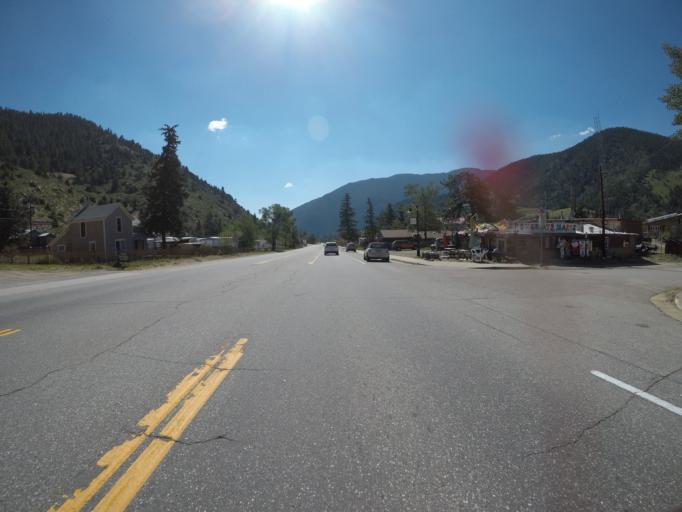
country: US
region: Colorado
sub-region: Clear Creek County
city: Georgetown
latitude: 39.7606
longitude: -105.6808
